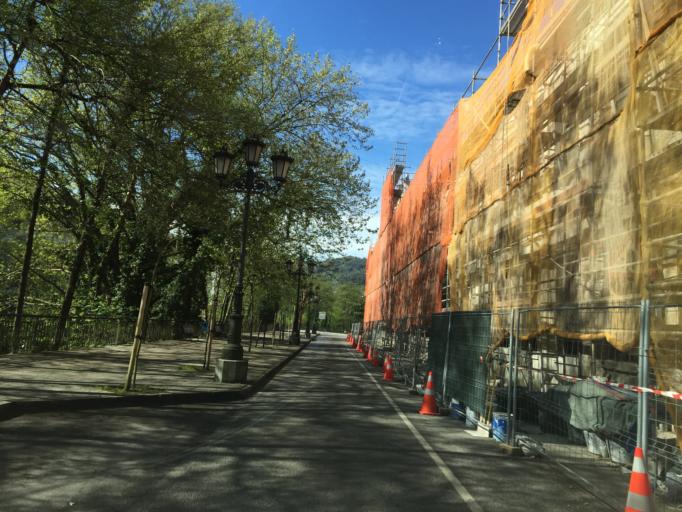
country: ES
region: Asturias
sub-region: Province of Asturias
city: Proaza
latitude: 43.3450
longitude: -5.9729
